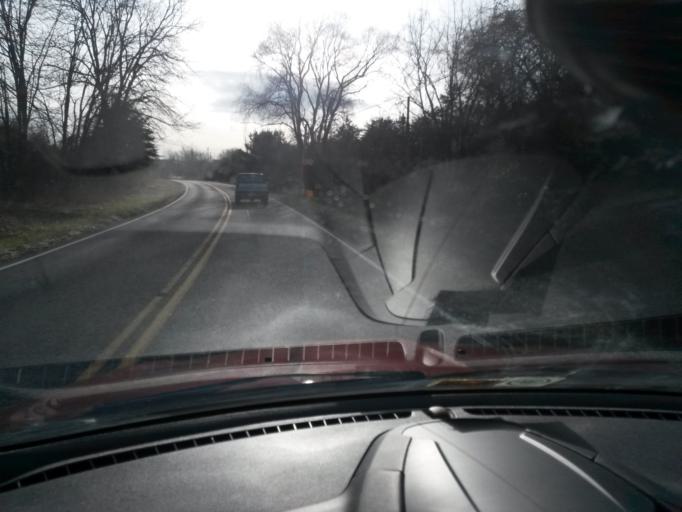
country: US
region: Virginia
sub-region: Rockbridge County
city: East Lexington
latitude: 38.0684
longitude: -79.4032
